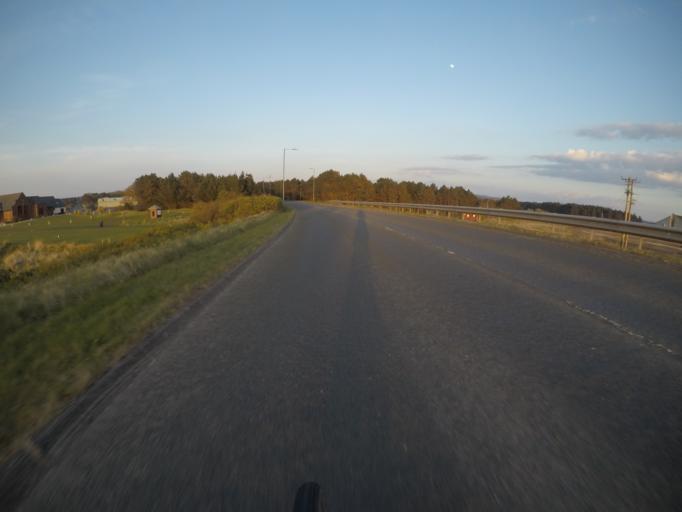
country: GB
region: Scotland
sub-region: North Ayrshire
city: Irvine
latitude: 55.5894
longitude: -4.6637
